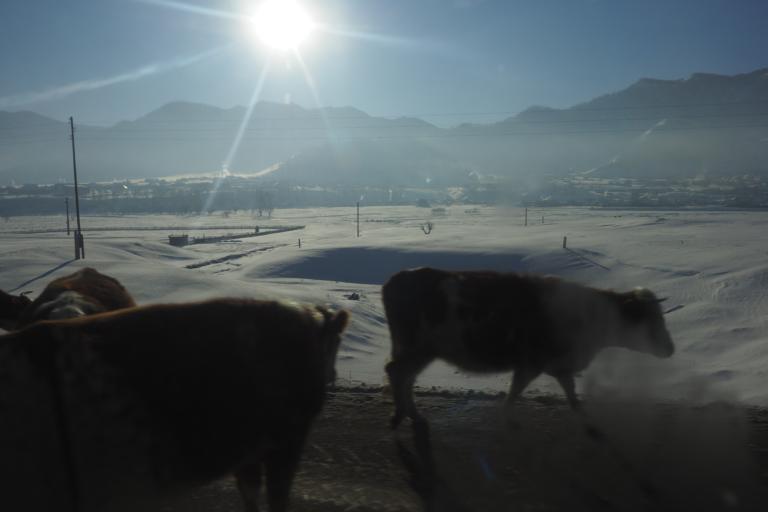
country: RU
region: Altay
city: Onguday
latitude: 50.7450
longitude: 86.1570
